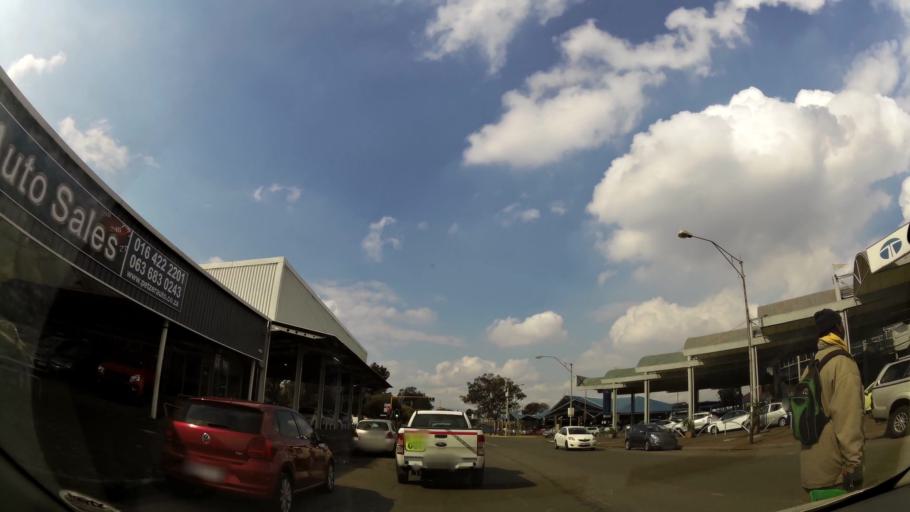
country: ZA
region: Gauteng
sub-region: Sedibeng District Municipality
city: Vereeniging
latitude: -26.6685
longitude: 27.9346
